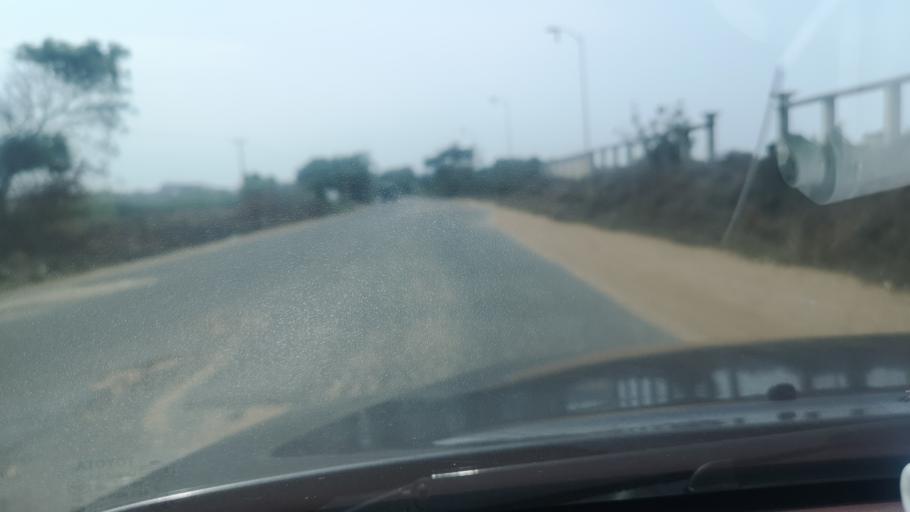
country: GH
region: Greater Accra
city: Nungua
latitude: 5.6134
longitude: -0.0563
